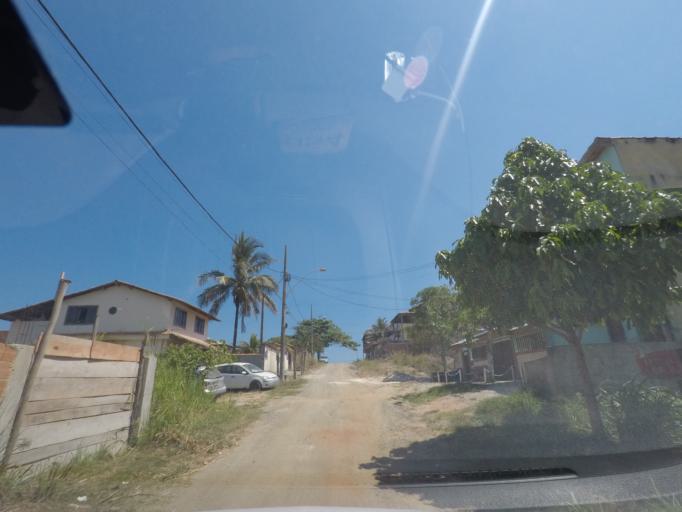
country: BR
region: Rio de Janeiro
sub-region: Marica
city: Marica
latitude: -22.9730
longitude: -42.9189
